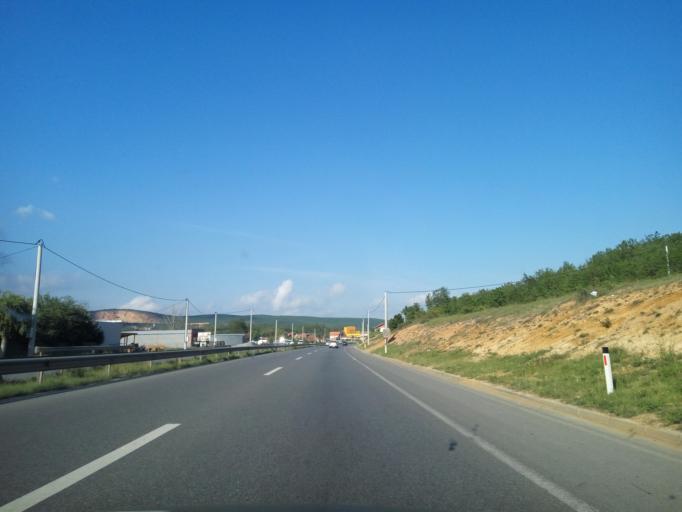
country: XK
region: Pristina
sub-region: Komuna e Drenasit
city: Glogovac
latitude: 42.6002
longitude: 20.9392
